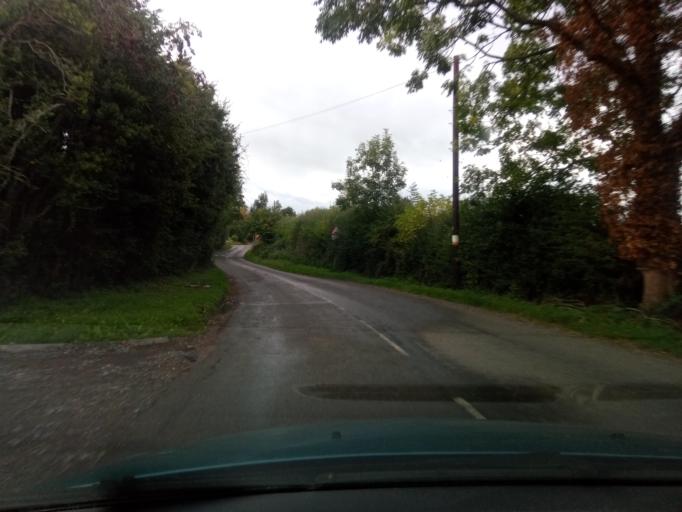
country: GB
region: England
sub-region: Leicestershire
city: Sileby
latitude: 52.7512
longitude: -1.0809
